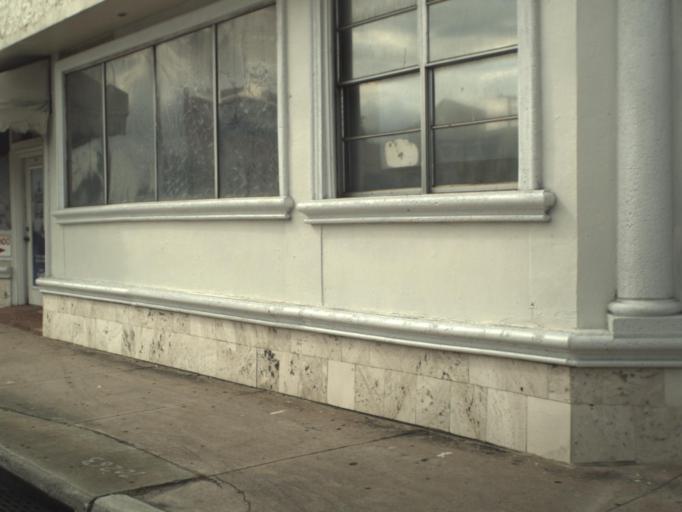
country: US
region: Florida
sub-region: Miami-Dade County
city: West Miami
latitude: 25.7633
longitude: -80.3010
